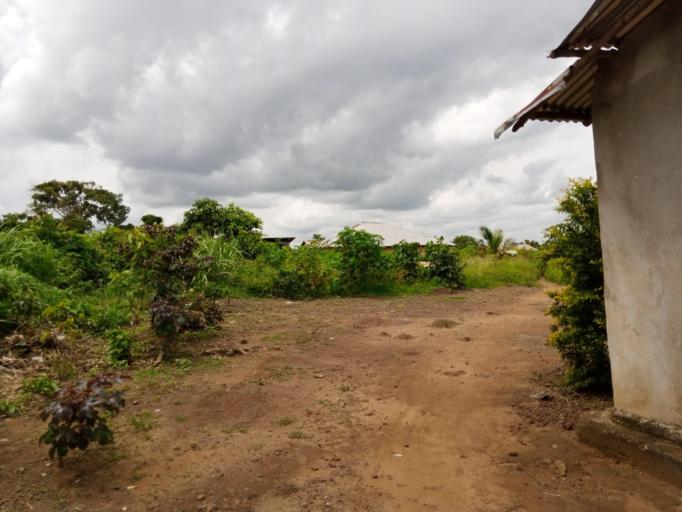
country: SL
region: Southern Province
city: Moyamba
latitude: 8.1624
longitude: -12.4230
